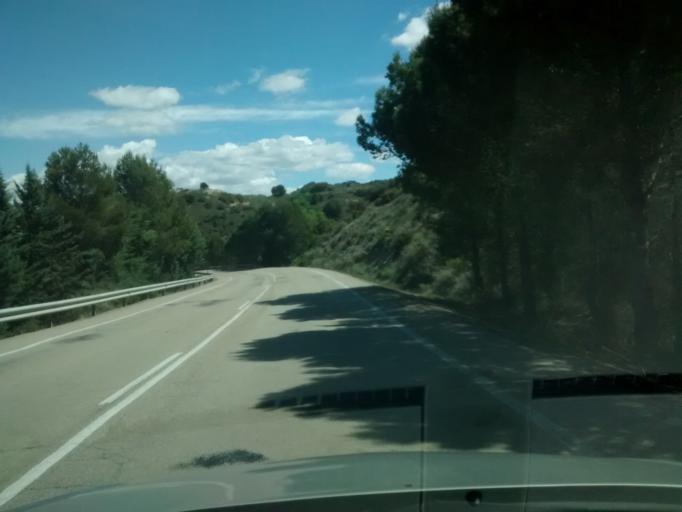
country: ES
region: Aragon
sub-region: Provincia de Huesca
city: Alcubierre
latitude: 41.8209
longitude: -0.5124
